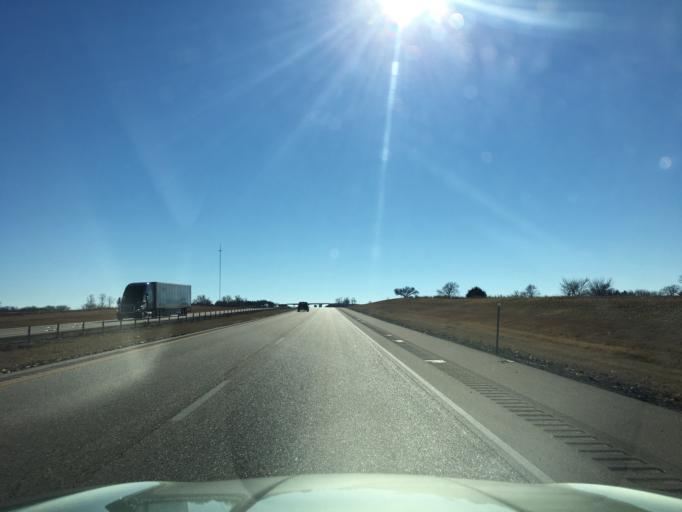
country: US
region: Oklahoma
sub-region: Kay County
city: Blackwell
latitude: 36.8760
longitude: -97.3503
